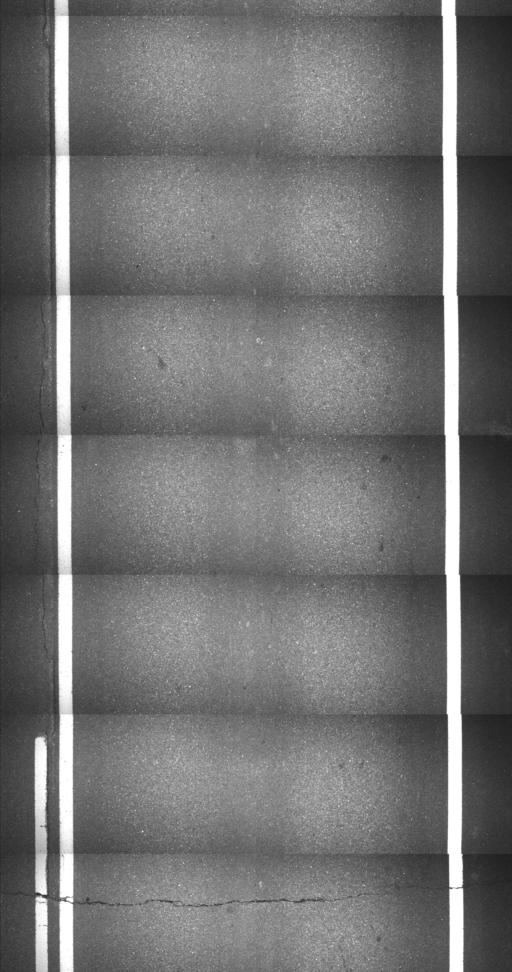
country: US
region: New Hampshire
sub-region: Cheshire County
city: Westmoreland
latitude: 43.0236
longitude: -72.4690
